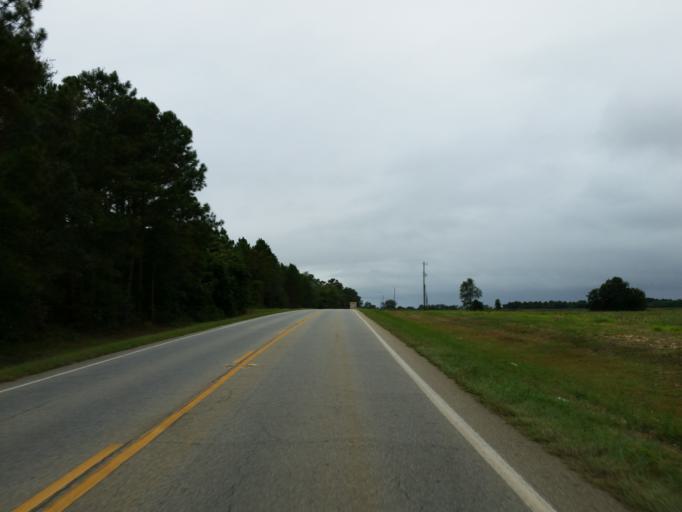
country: US
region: Georgia
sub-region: Cook County
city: Adel
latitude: 31.1322
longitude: -83.3704
